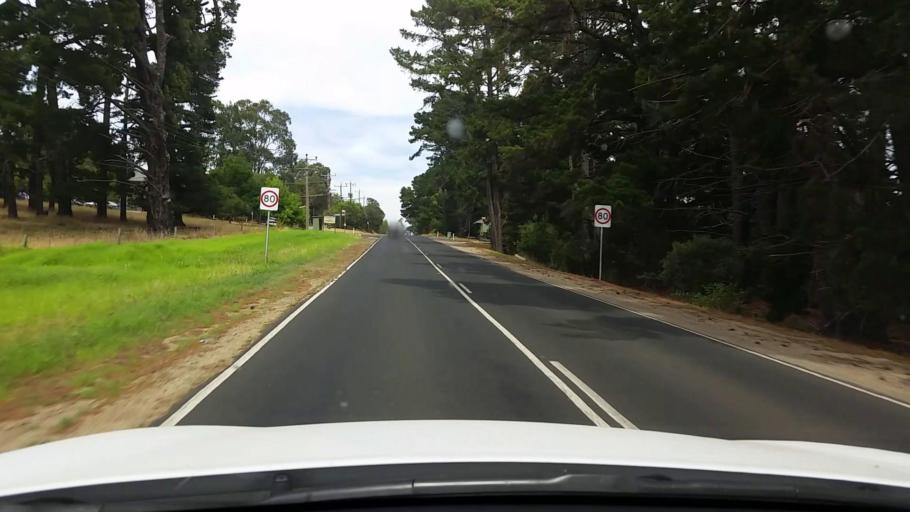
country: AU
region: Victoria
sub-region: Mornington Peninsula
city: Merricks
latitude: -38.4152
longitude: 145.0523
